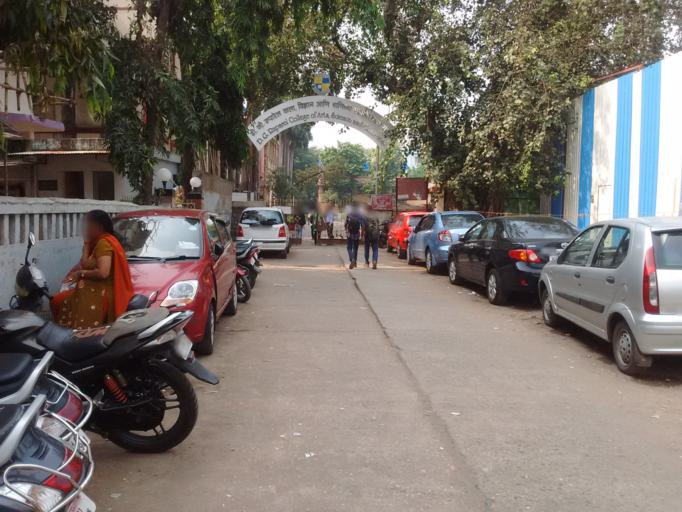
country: IN
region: Maharashtra
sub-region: Mumbai Suburban
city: Mumbai
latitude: 19.0279
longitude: 72.8461
